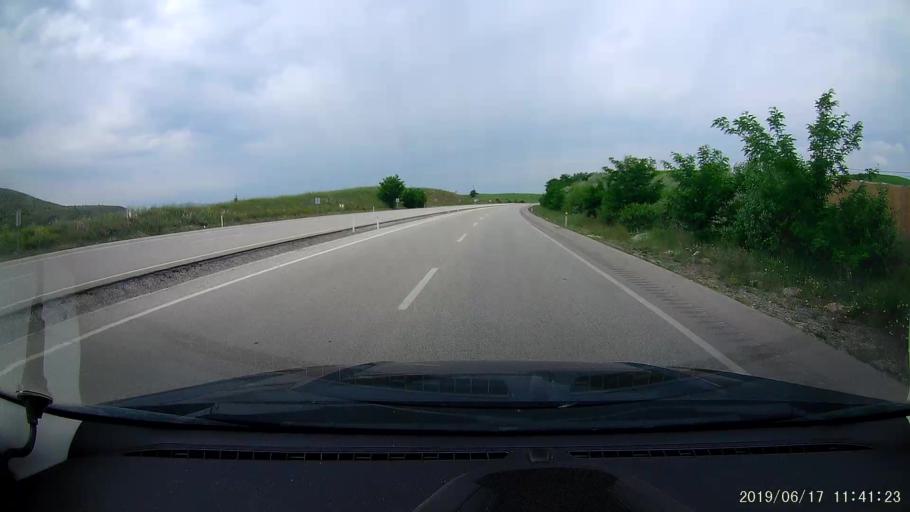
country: TR
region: Cankiri
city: Kursunlu
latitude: 40.8303
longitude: 33.3266
